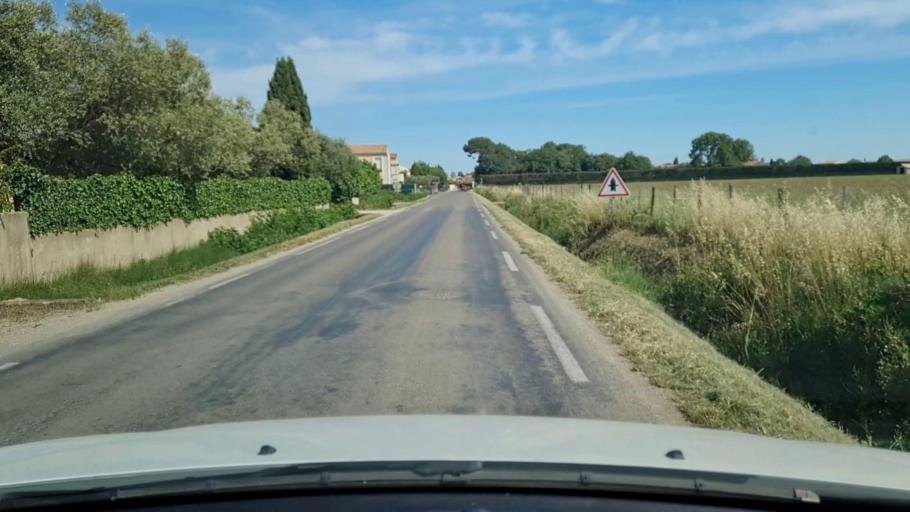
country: FR
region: Languedoc-Roussillon
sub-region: Departement de l'Herault
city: Marsillargues
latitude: 43.6276
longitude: 4.1979
